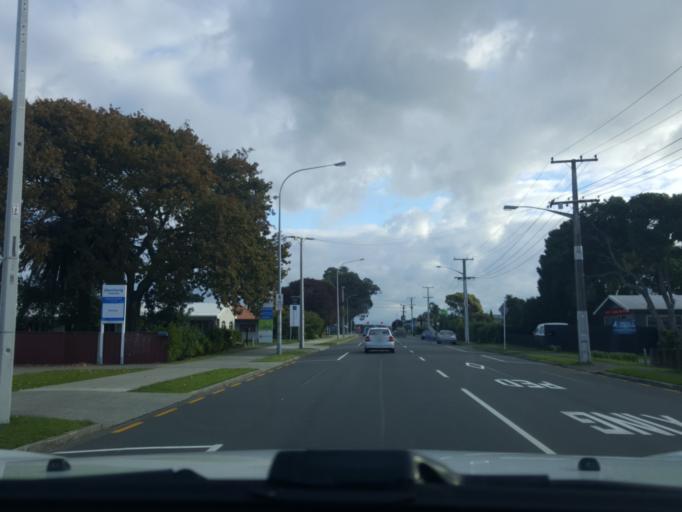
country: NZ
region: Bay of Plenty
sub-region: Tauranga City
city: Tauranga
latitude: -37.6736
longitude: 176.2295
